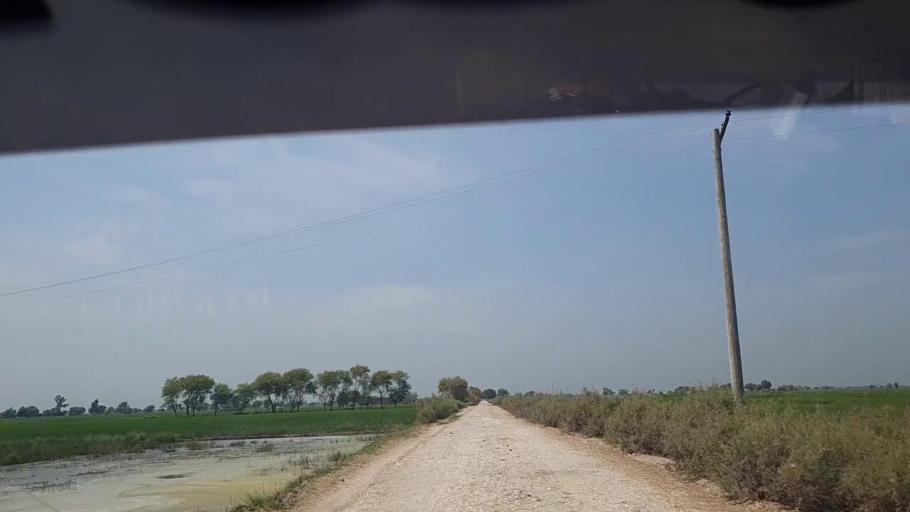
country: PK
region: Sindh
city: Thul
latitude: 28.1712
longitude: 68.7527
